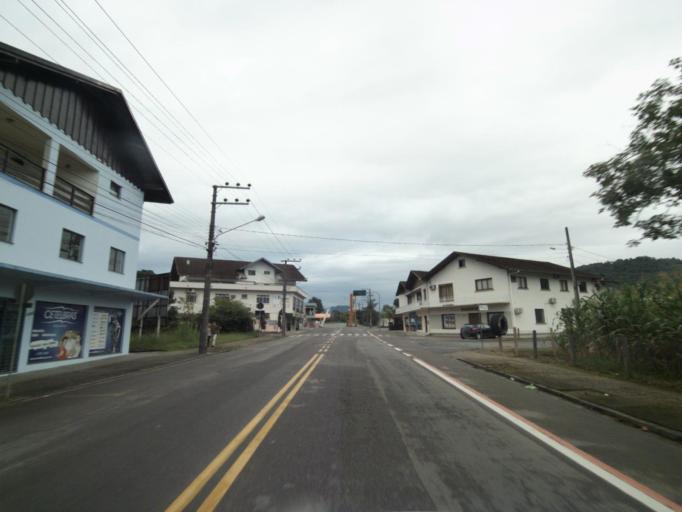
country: BR
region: Santa Catarina
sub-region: Pomerode
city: Pomerode
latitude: -26.7268
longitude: -49.1735
